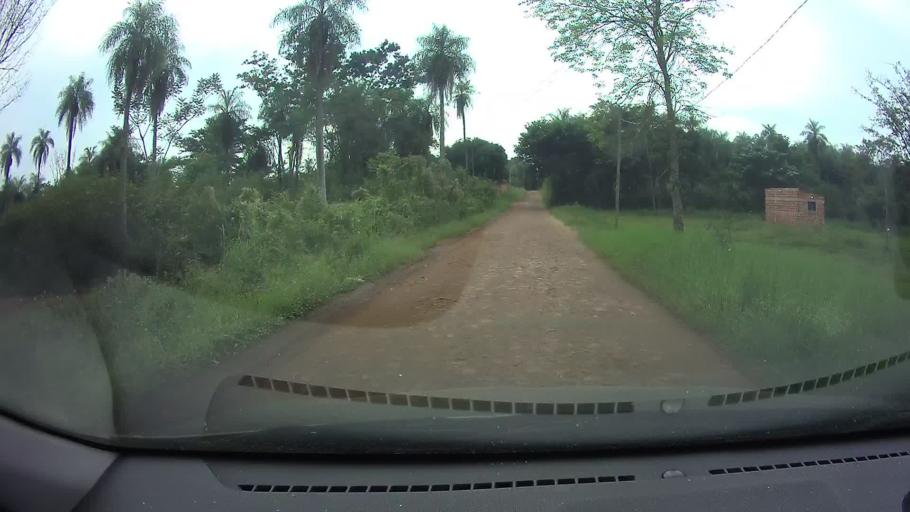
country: PY
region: Central
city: Limpio
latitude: -25.2391
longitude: -57.4622
